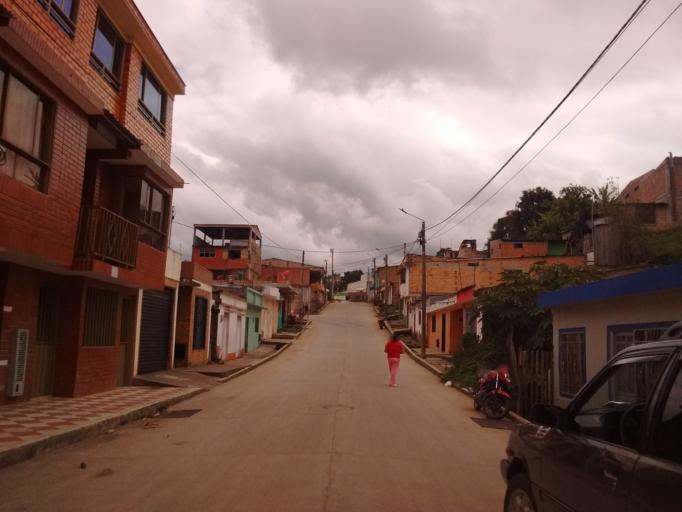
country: CO
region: Huila
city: Isnos
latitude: 1.9316
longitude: -76.2146
